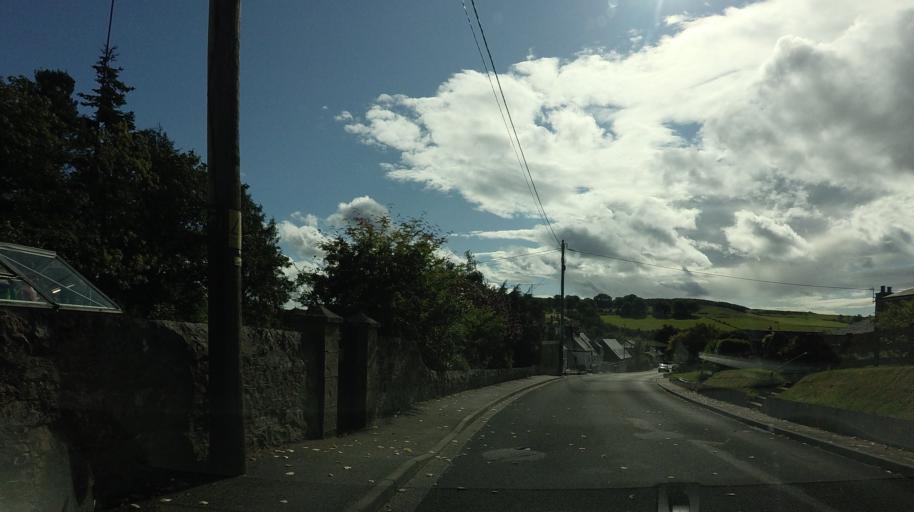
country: GB
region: Scotland
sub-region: Aberdeenshire
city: Torphins
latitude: 57.1306
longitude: -2.6898
